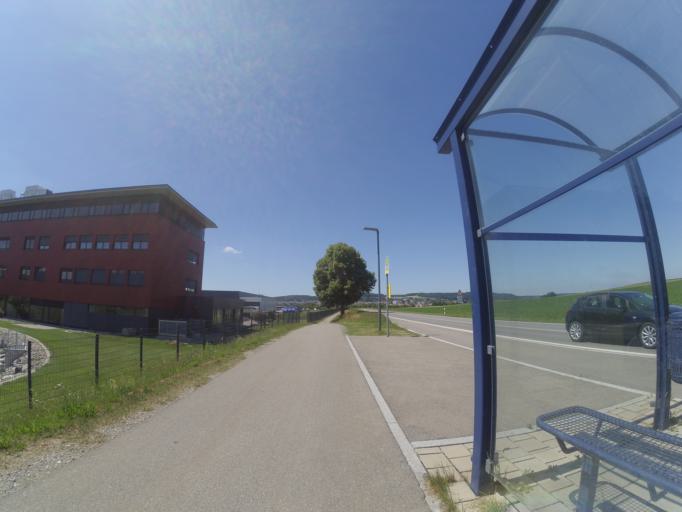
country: DE
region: Baden-Wuerttemberg
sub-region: Tuebingen Region
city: Aulendorf
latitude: 47.9394
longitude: 9.6532
